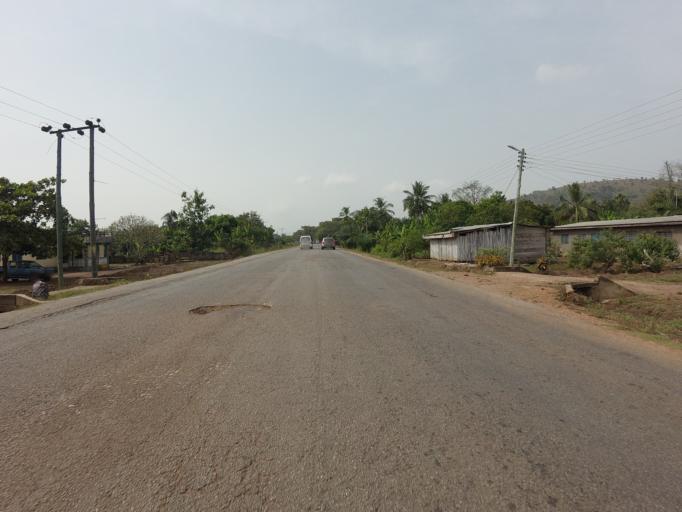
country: GH
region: Volta
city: Ho
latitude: 6.3650
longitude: 0.1824
